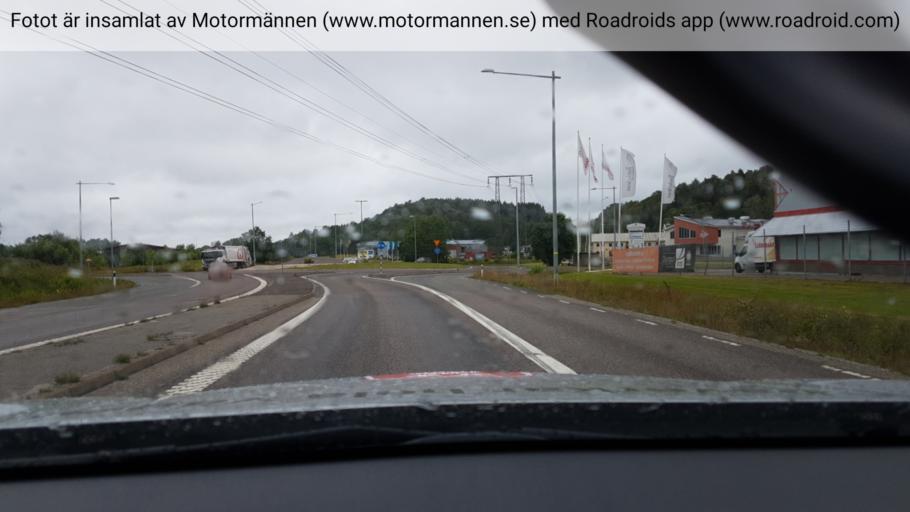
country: SE
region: Vaestra Goetaland
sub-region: Stenungsunds Kommun
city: Stenungsund
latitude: 58.0626
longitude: 11.8704
